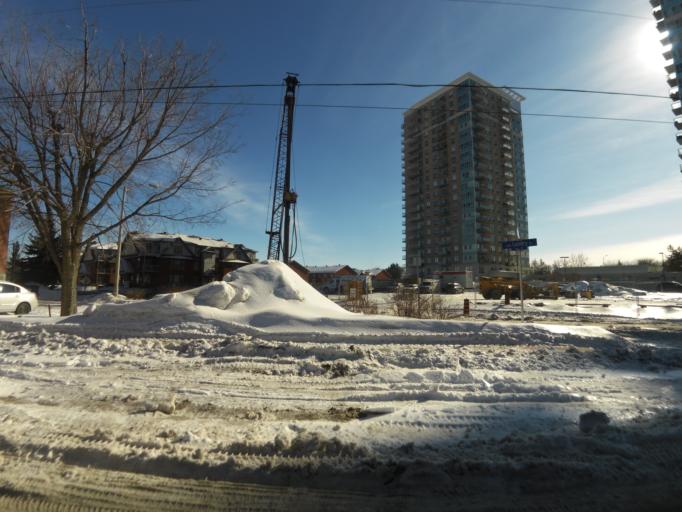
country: CA
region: Ontario
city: Ottawa
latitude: 45.4386
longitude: -75.6719
